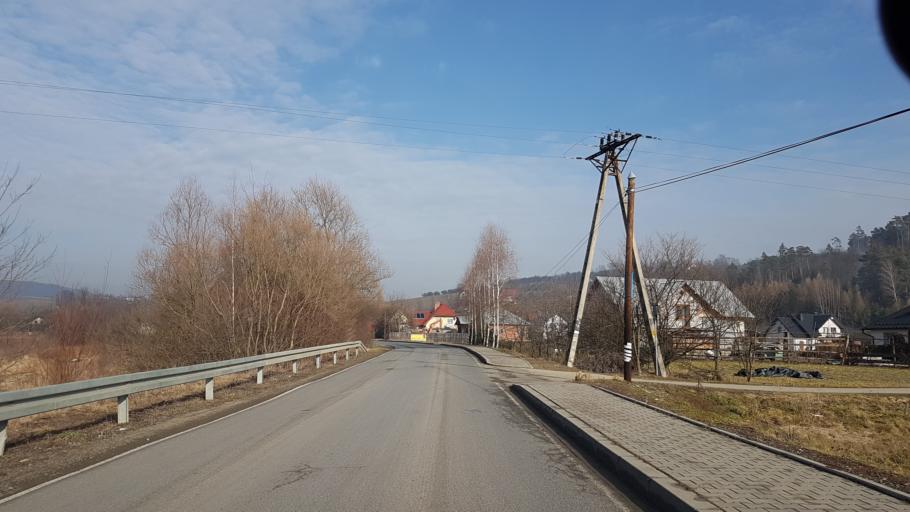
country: PL
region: Lesser Poland Voivodeship
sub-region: Powiat nowosadecki
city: Olszana
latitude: 49.5886
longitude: 20.5354
